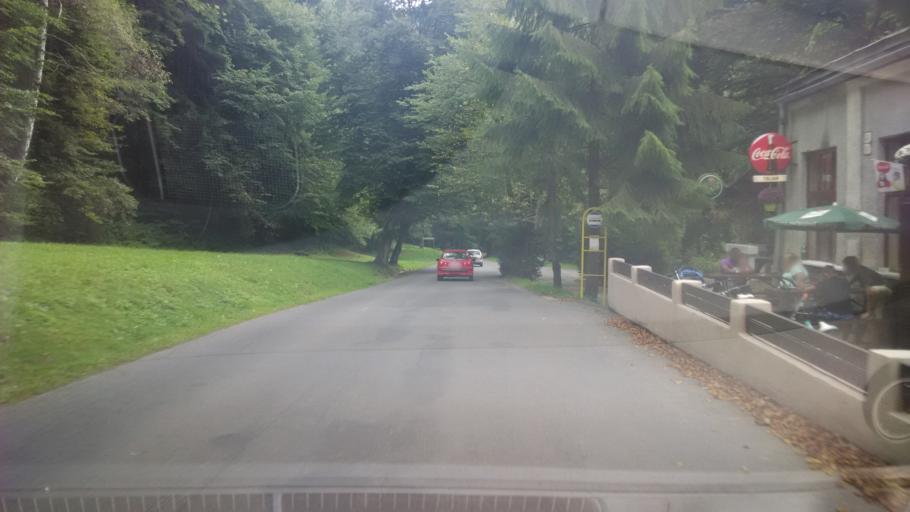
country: SK
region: Banskobystricky
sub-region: Okres Ziar nad Hronom
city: Kremnica
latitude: 48.7088
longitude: 18.9488
